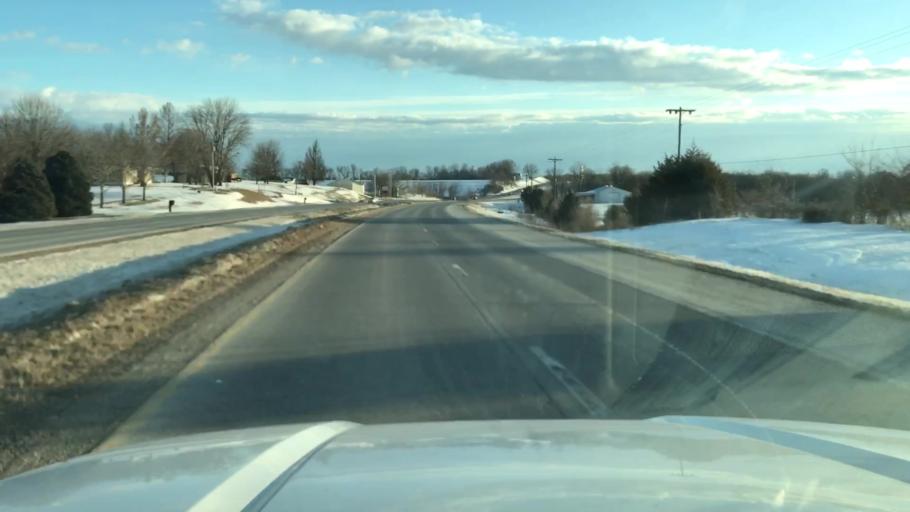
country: US
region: Missouri
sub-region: Andrew County
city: Country Club Village
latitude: 39.8683
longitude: -94.8084
